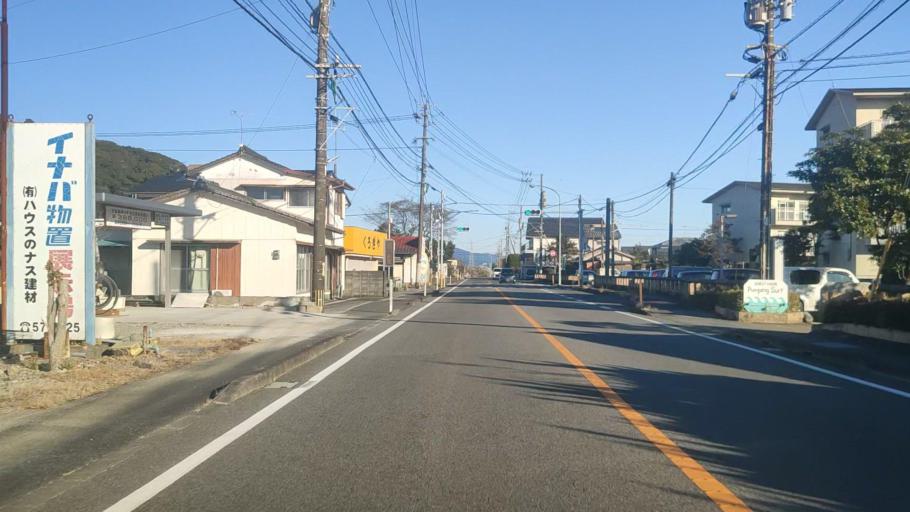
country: JP
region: Miyazaki
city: Nobeoka
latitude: 32.3847
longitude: 131.6275
